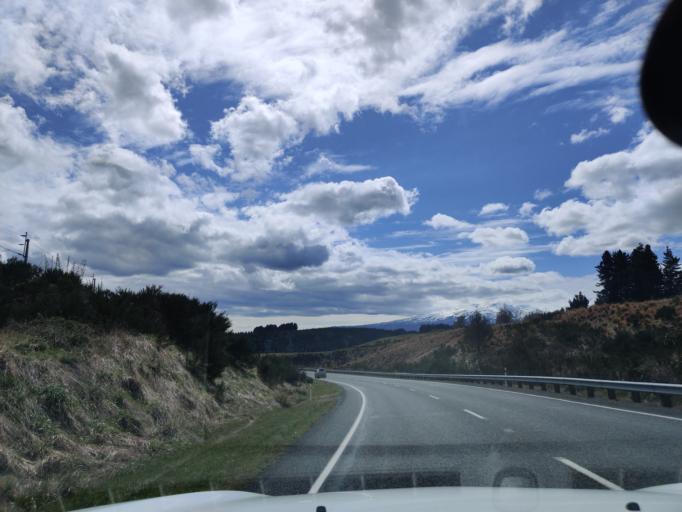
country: NZ
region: Manawatu-Wanganui
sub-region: Ruapehu District
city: Waiouru
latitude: -39.4670
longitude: 175.6641
